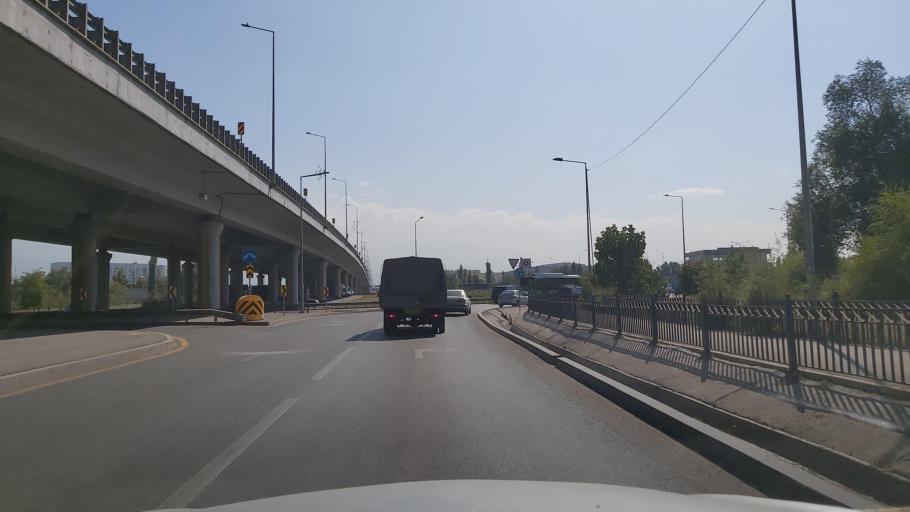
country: KZ
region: Almaty Qalasy
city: Almaty
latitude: 43.3045
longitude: 76.8961
